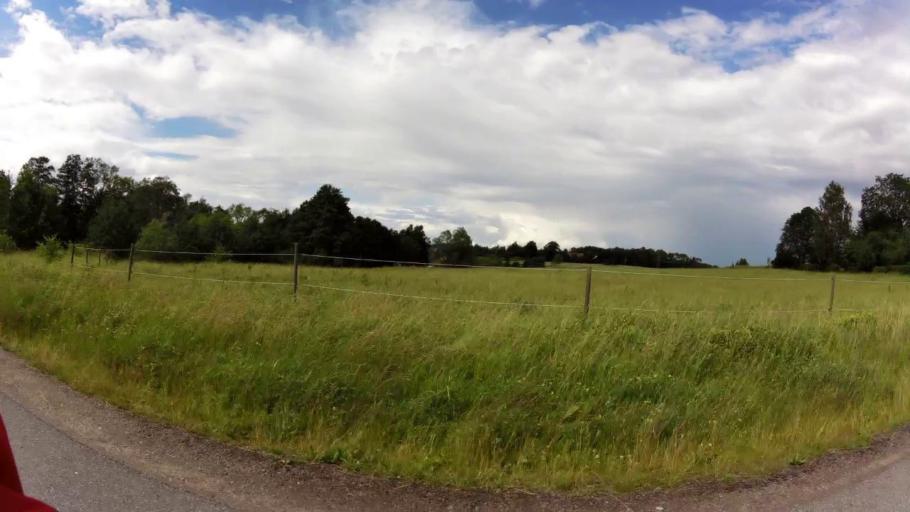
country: SE
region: OEstergoetland
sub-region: Linkopings Kommun
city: Linkoping
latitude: 58.3961
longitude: 15.6808
